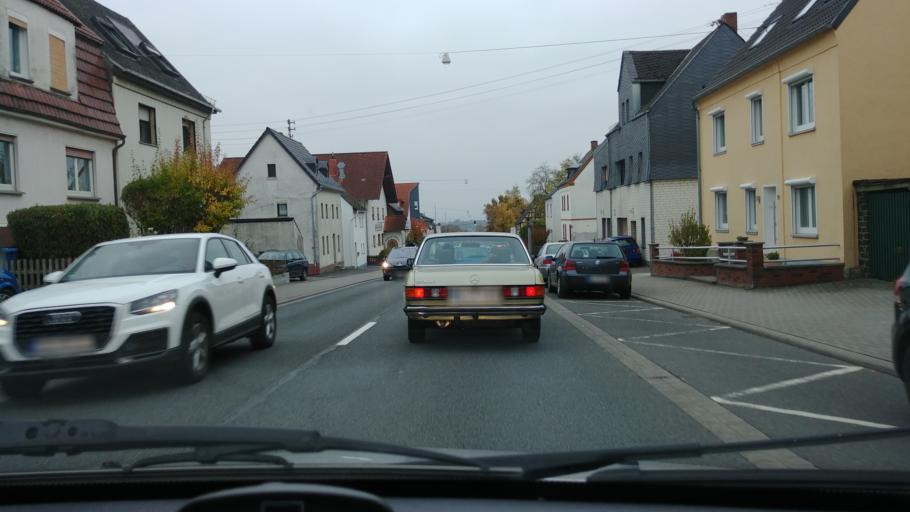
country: DE
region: Hesse
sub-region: Regierungsbezirk Giessen
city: Elz
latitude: 50.4751
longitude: 8.0586
